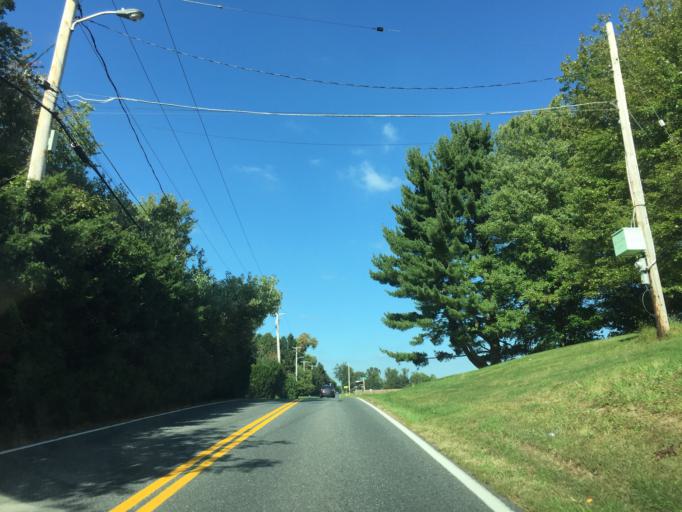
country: US
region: Maryland
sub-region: Harford County
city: Fallston
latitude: 39.5340
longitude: -76.4458
